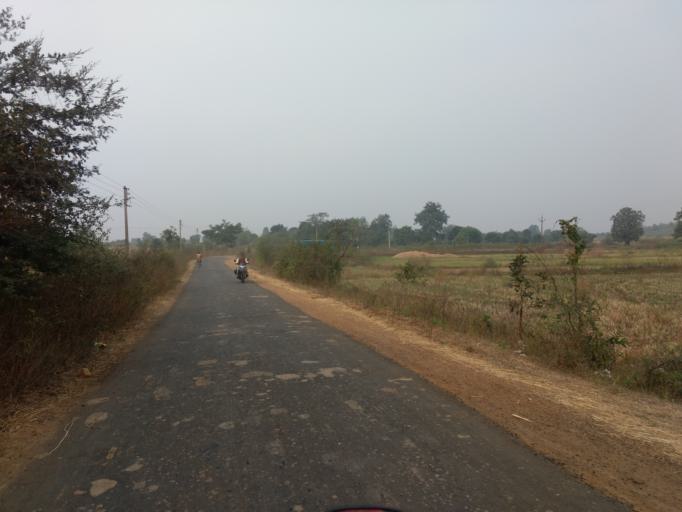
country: IN
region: Maharashtra
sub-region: Chandrapur
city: Mul
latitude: 19.9222
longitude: 79.9277
